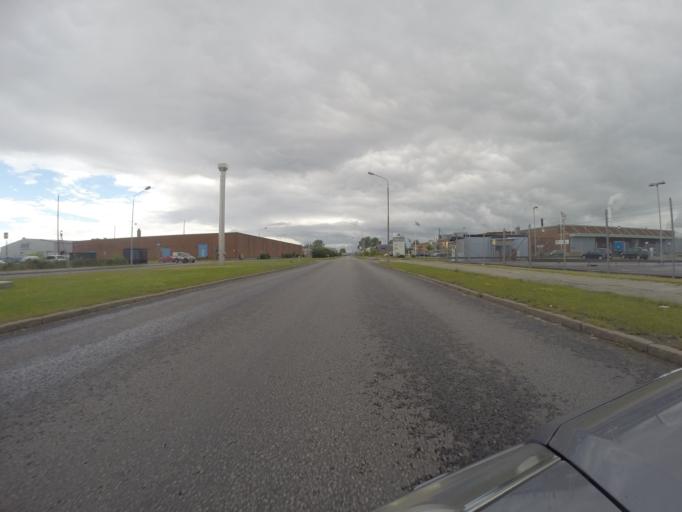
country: SE
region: Skane
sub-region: Burlovs Kommun
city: Arloev
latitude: 55.6262
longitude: 13.0372
